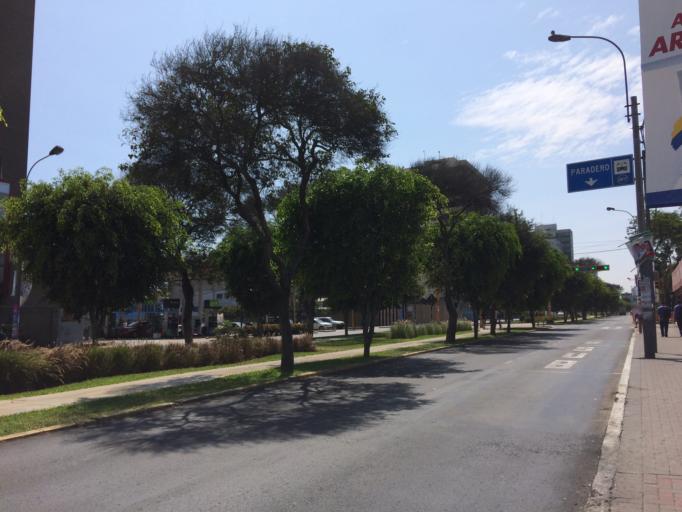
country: PE
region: Lima
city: Lima
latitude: -12.0740
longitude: -77.0359
